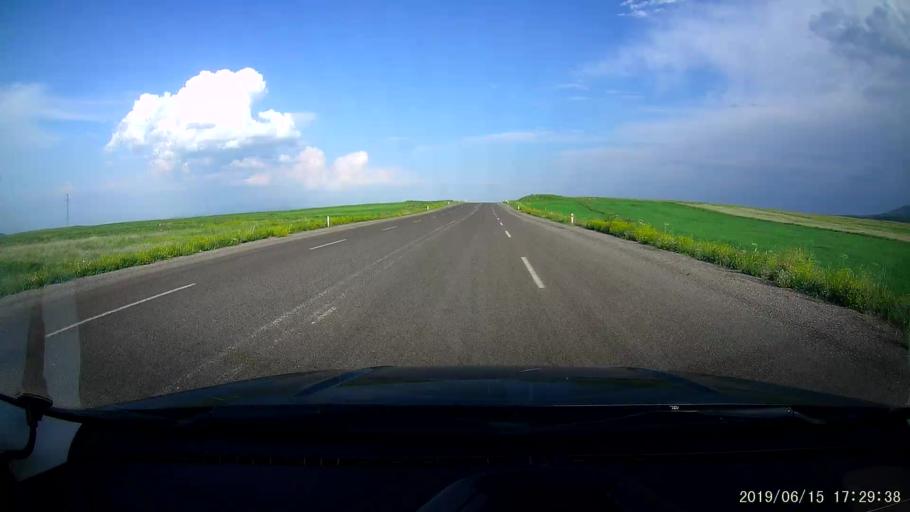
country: TR
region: Kars
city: Basgedikler
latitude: 40.5883
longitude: 43.4555
